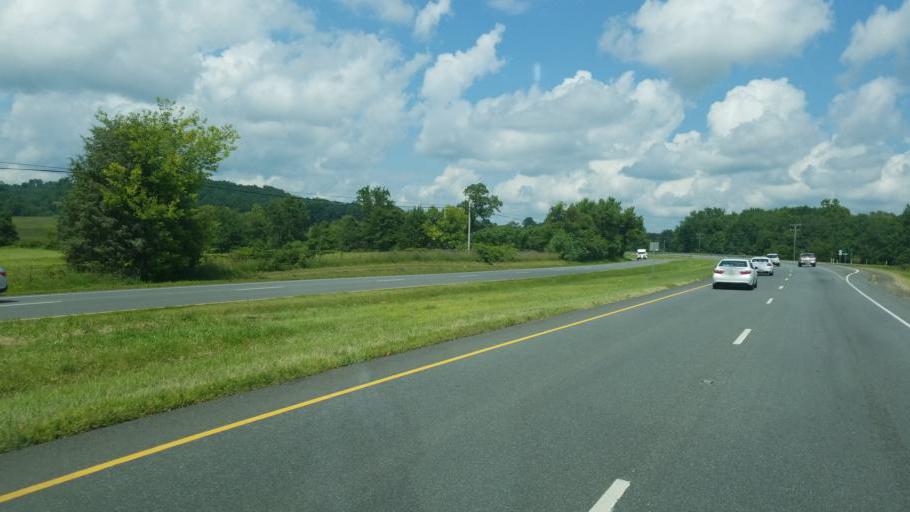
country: US
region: Virginia
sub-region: Fauquier County
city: Marshall
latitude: 38.8037
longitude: -77.8138
